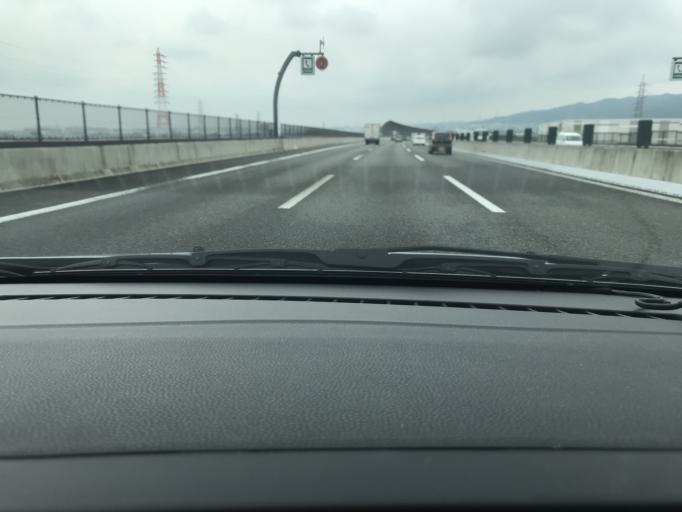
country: JP
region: Osaka
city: Hirakata
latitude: 34.7772
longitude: 135.6666
